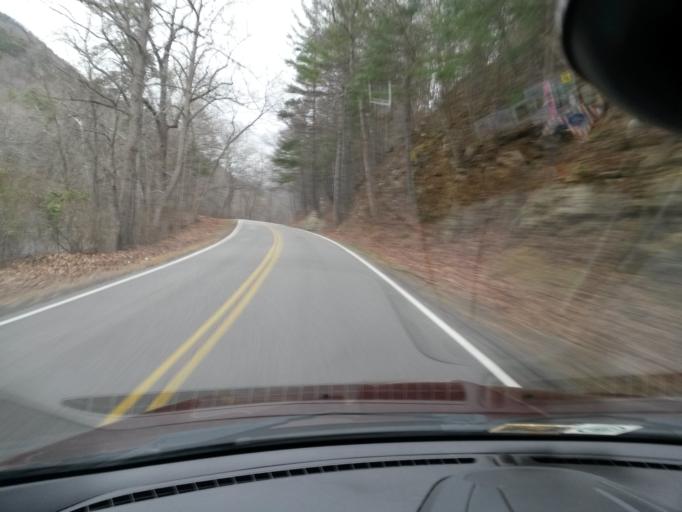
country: US
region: Virginia
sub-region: Rockbridge County
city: East Lexington
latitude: 37.9671
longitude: -79.4984
